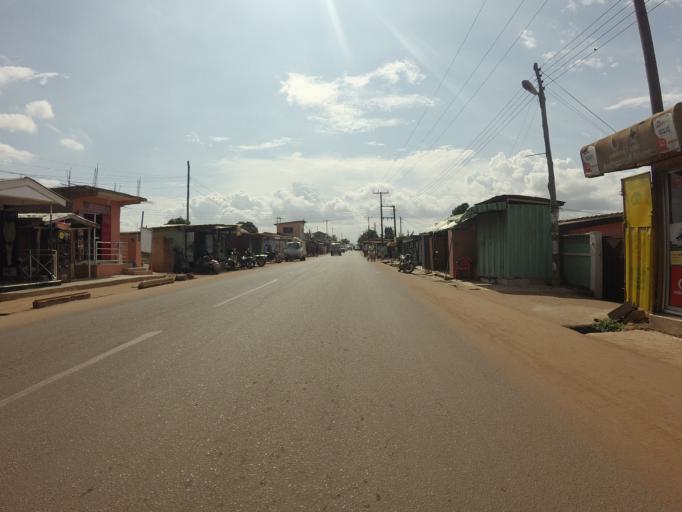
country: GH
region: Greater Accra
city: Medina Estates
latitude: 5.6788
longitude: -0.1769
